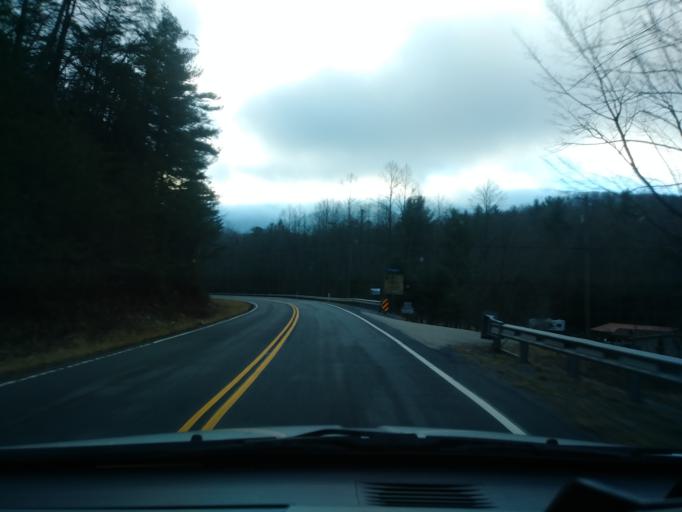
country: US
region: Tennessee
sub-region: Unicoi County
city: Unicoi
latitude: 36.1750
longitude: -82.3137
